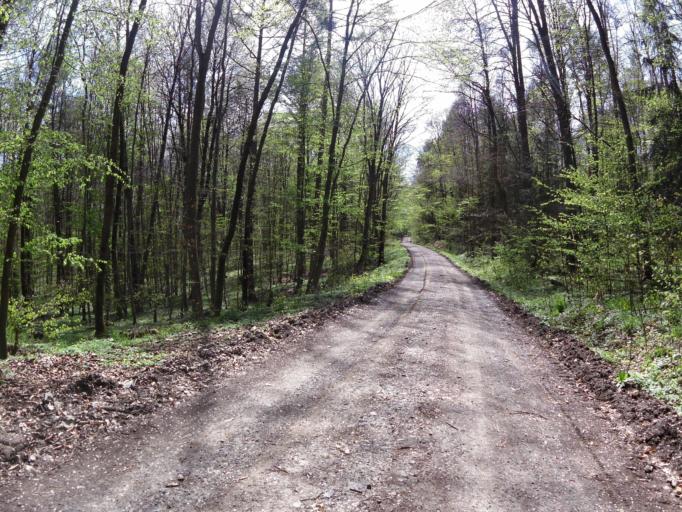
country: DE
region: Bavaria
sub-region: Regierungsbezirk Unterfranken
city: Rimpar
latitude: 49.8649
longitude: 9.9850
